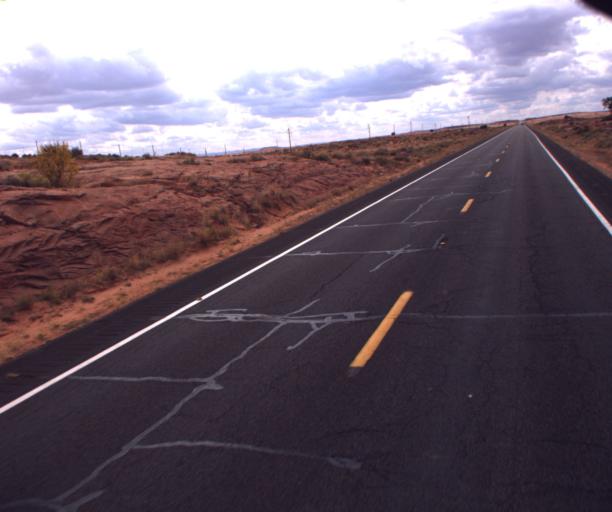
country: US
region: Arizona
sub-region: Navajo County
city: Kayenta
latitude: 36.9363
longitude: -109.7400
